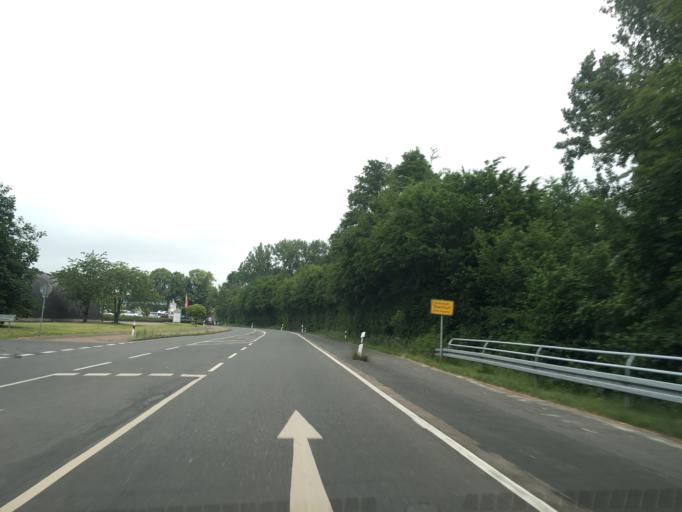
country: DE
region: North Rhine-Westphalia
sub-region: Regierungsbezirk Munster
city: Steinfurt
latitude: 52.1383
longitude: 7.3433
